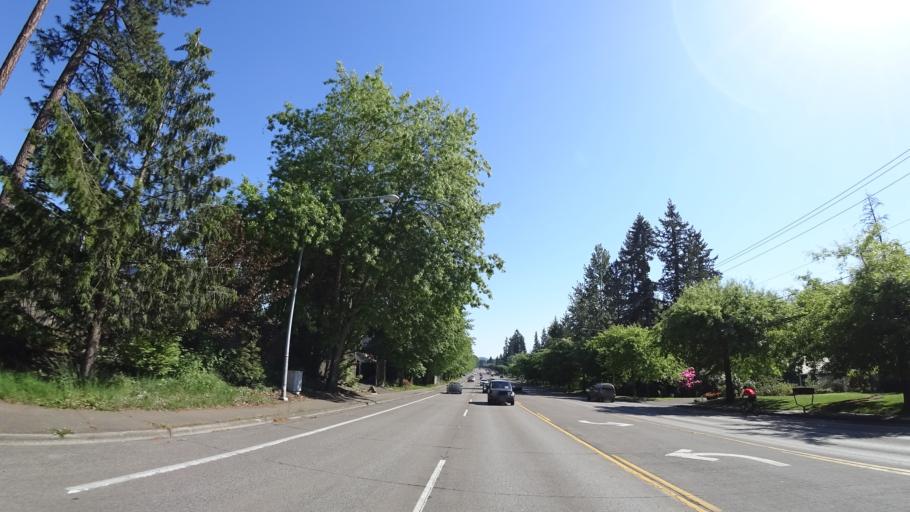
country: US
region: Oregon
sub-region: Washington County
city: Aloha
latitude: 45.5093
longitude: -122.8674
